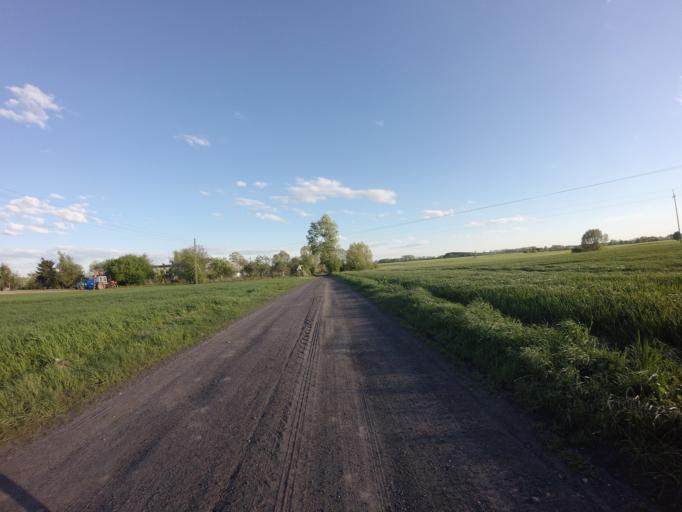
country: PL
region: West Pomeranian Voivodeship
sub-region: Powiat choszczenski
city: Choszczno
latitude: 53.1426
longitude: 15.4303
